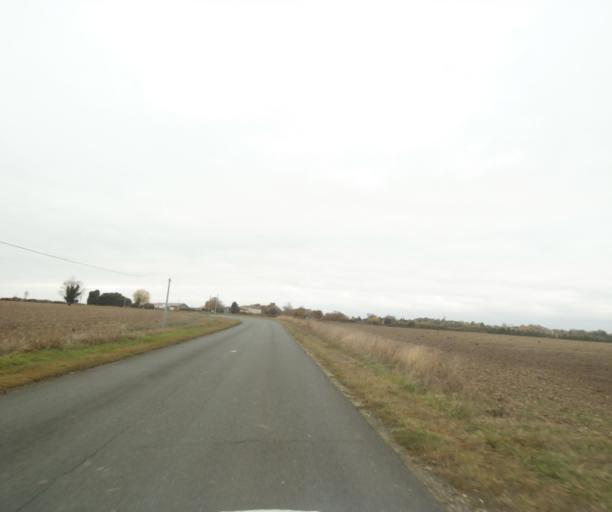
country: FR
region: Poitou-Charentes
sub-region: Departement de la Charente-Maritime
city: Saintes
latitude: 45.7308
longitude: -0.6657
